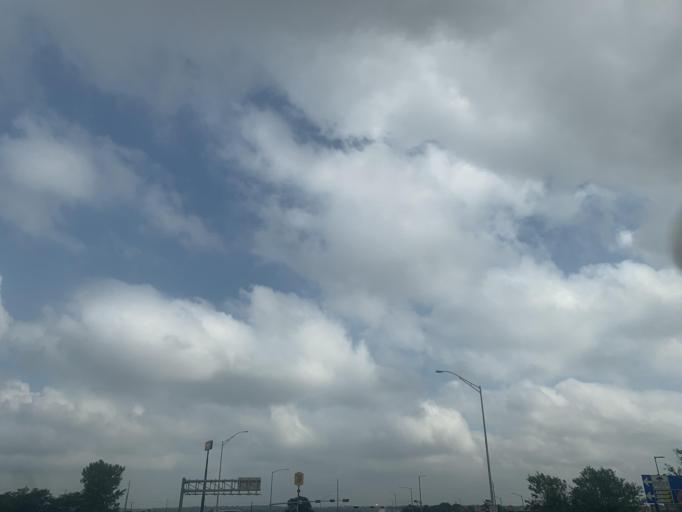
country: US
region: Nebraska
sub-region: Sarpy County
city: Chalco
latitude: 41.1639
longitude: -96.1388
